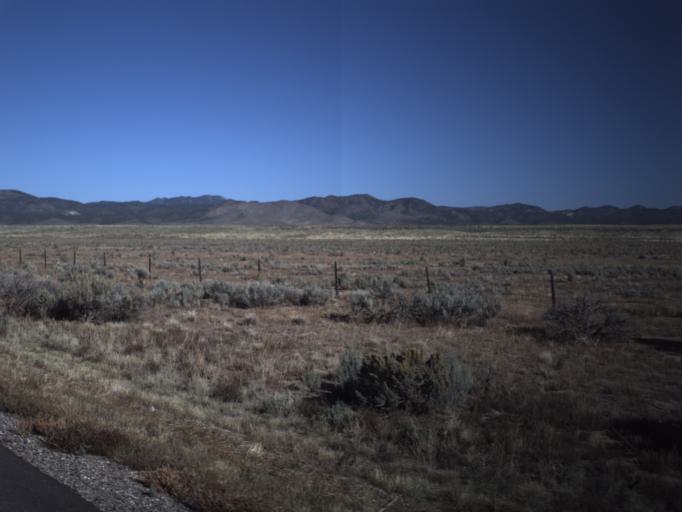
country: US
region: Utah
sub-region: Washington County
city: Enterprise
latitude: 37.7819
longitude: -113.8623
